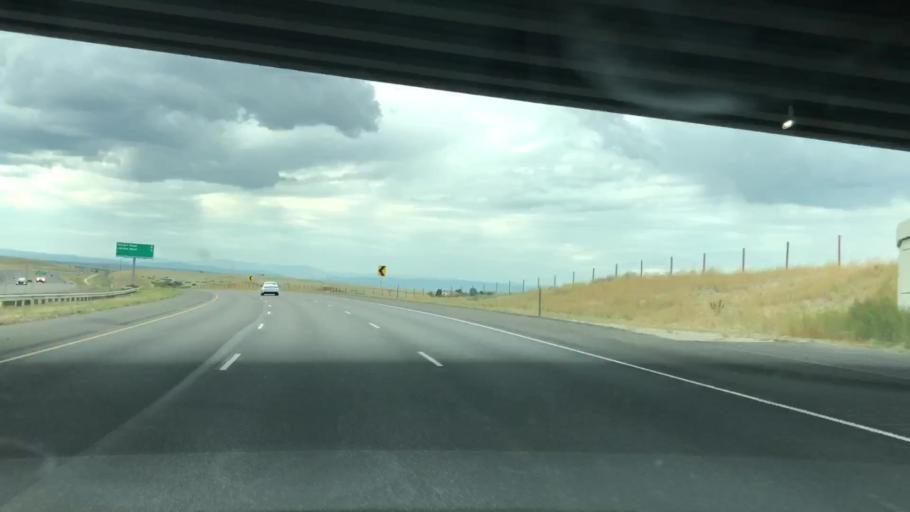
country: US
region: Colorado
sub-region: Douglas County
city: Parker
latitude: 39.5766
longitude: -104.7446
